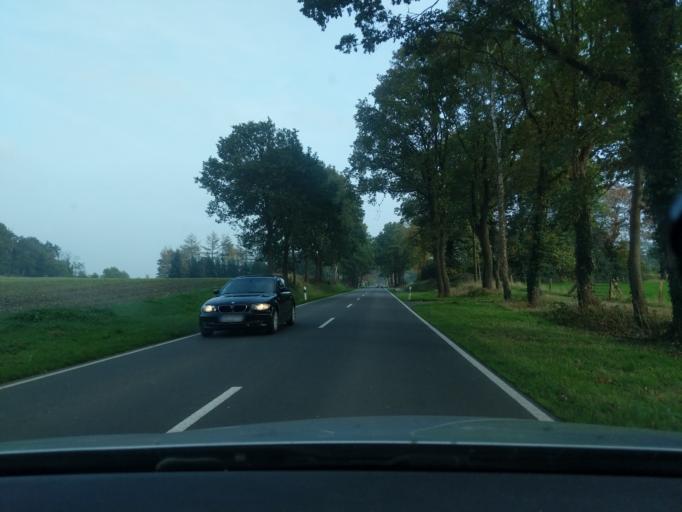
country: DE
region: Lower Saxony
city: Lamstedt
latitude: 53.6342
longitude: 9.1221
